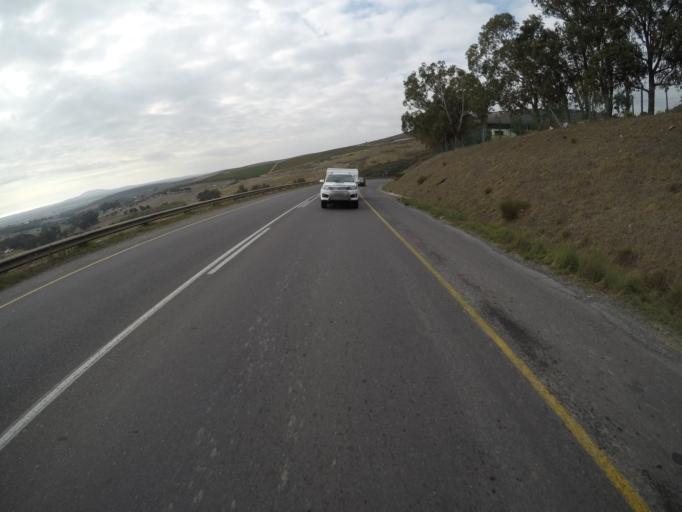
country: ZA
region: Western Cape
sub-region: City of Cape Town
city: Sunset Beach
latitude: -33.8288
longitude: 18.5890
